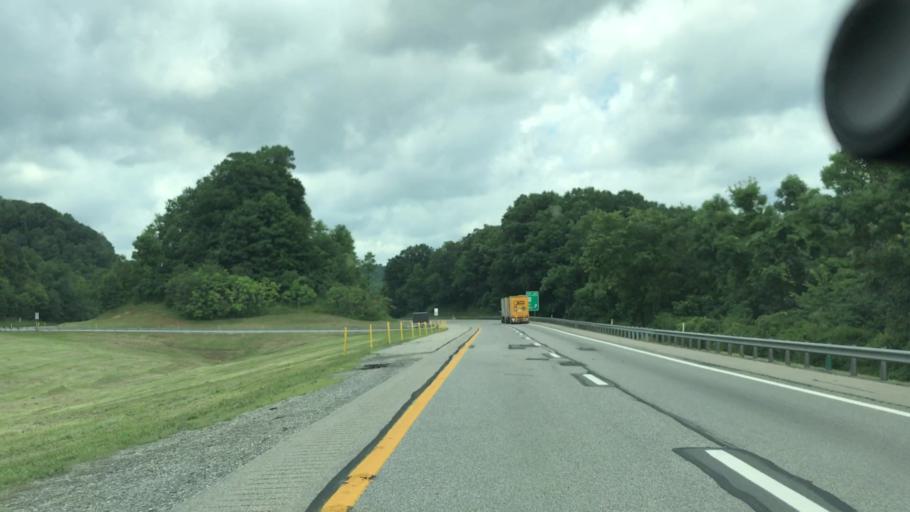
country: US
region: West Virginia
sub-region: Fayette County
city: Oak Hill
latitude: 37.9684
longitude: -81.2750
